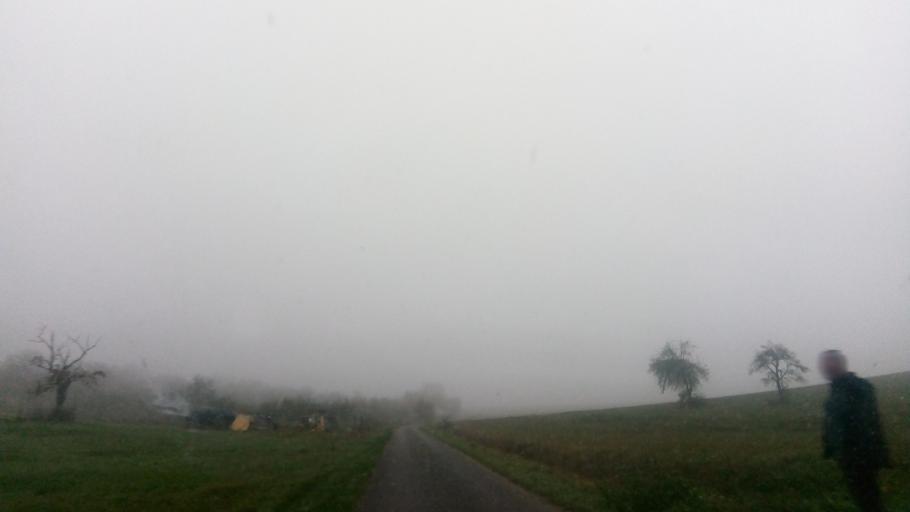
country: DE
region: Bavaria
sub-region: Regierungsbezirk Unterfranken
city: Uchtelhausen
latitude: 50.0943
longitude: 10.2425
